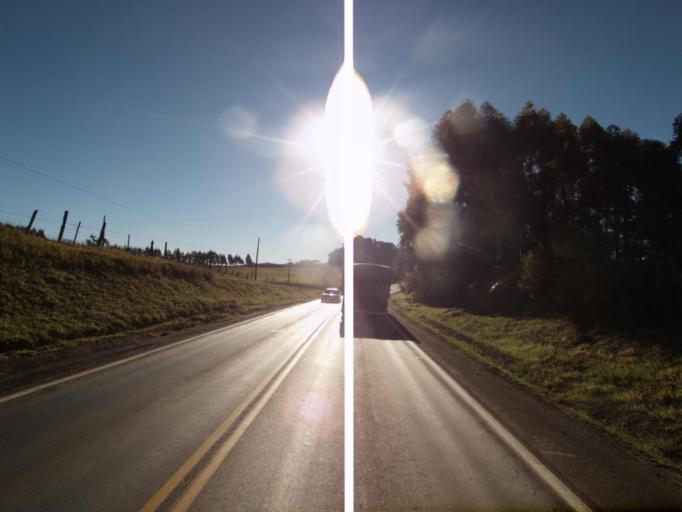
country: AR
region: Misiones
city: Bernardo de Irigoyen
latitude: -26.3047
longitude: -53.5508
